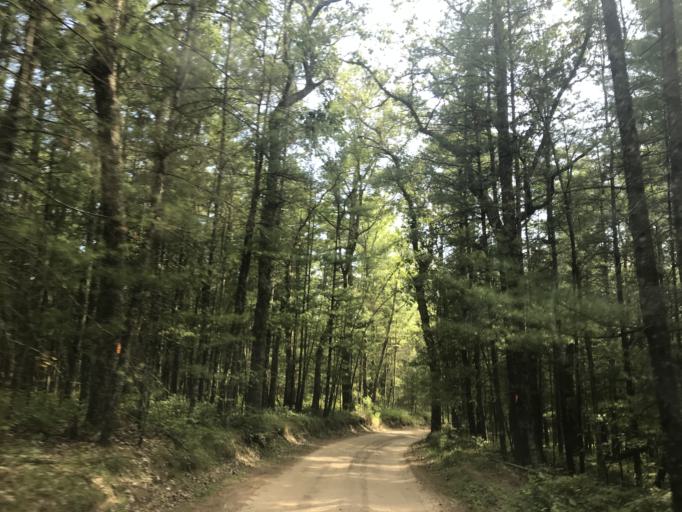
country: US
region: Michigan
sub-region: Newaygo County
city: Newaygo
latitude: 43.4545
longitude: -85.7611
